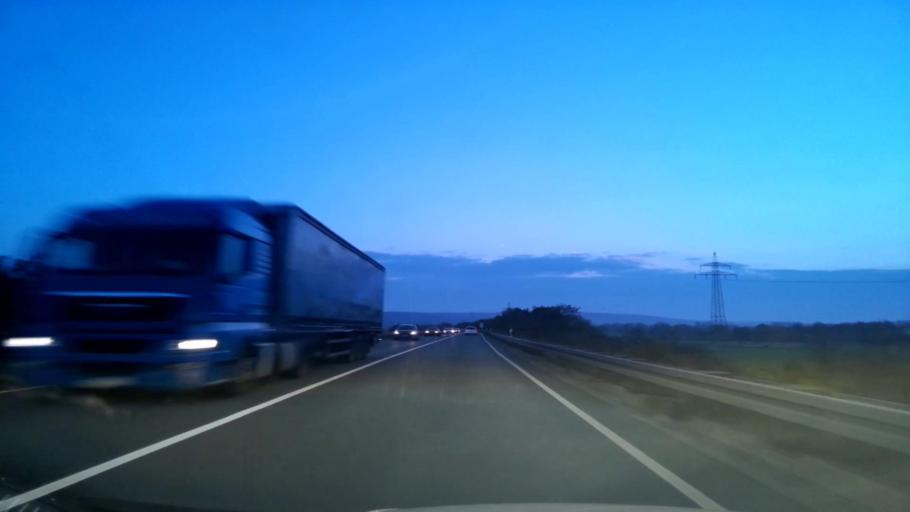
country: DE
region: Bavaria
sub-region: Upper Franconia
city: Strullendorf
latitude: 49.8483
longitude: 10.9543
